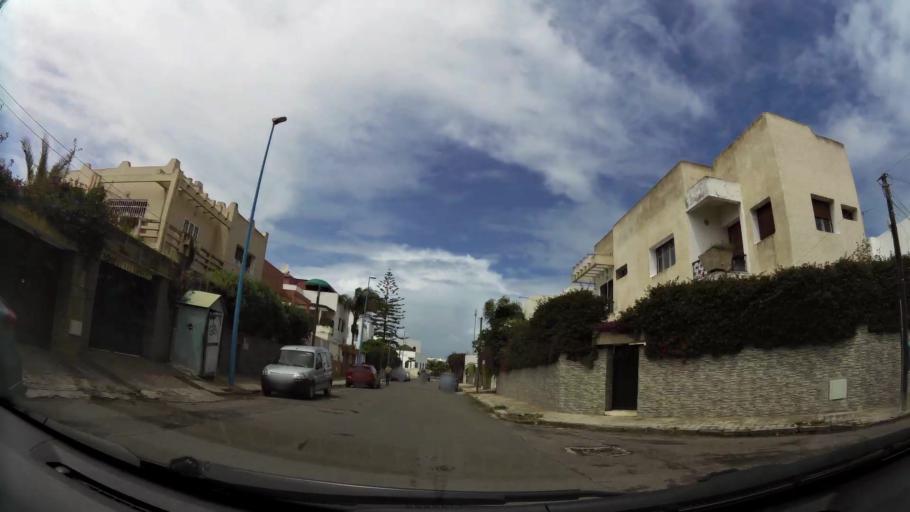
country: MA
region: Grand Casablanca
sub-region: Casablanca
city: Casablanca
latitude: 33.5656
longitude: -7.6338
